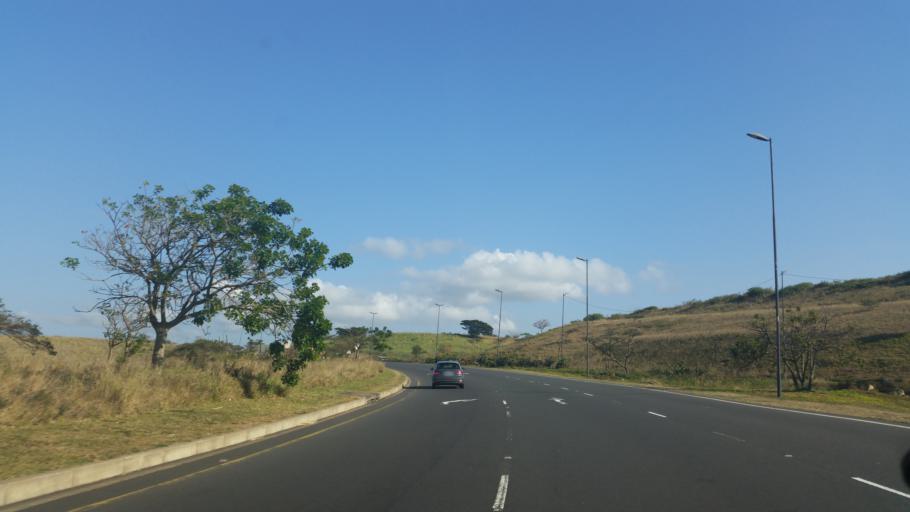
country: ZA
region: KwaZulu-Natal
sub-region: iLembe District Municipality
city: Ballitoville
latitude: -29.6258
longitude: 31.1178
